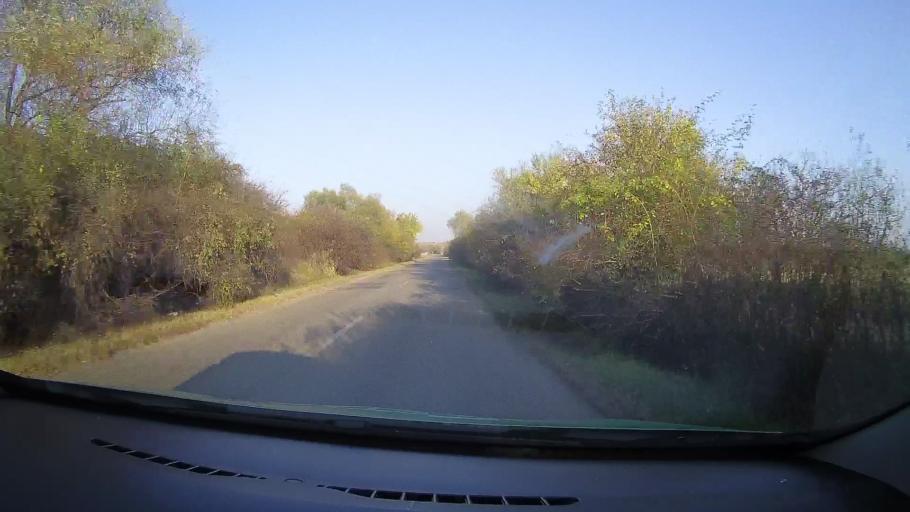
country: RO
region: Arad
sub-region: Comuna Silindia
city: Silindia
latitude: 46.3365
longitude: 21.9009
